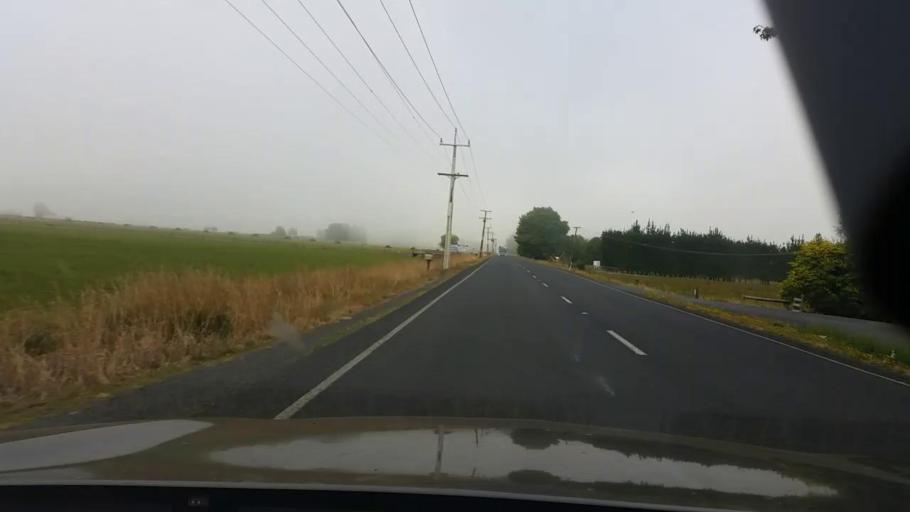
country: NZ
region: Waikato
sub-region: Hamilton City
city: Hamilton
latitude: -37.6272
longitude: 175.3196
